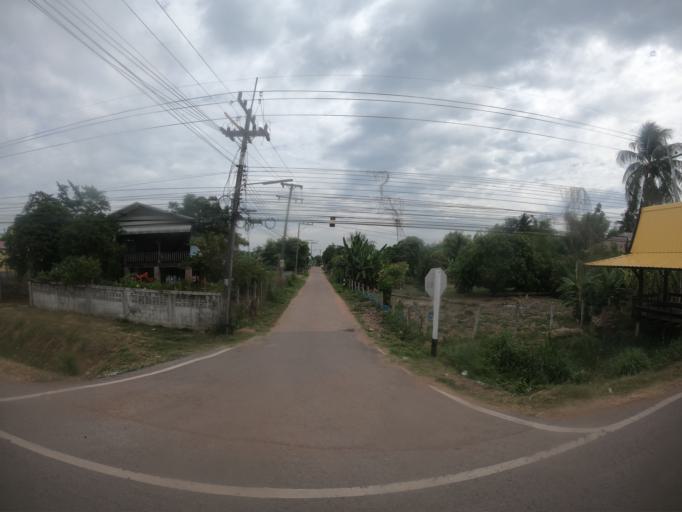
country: TH
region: Maha Sarakham
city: Kantharawichai
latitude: 16.3052
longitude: 103.2993
